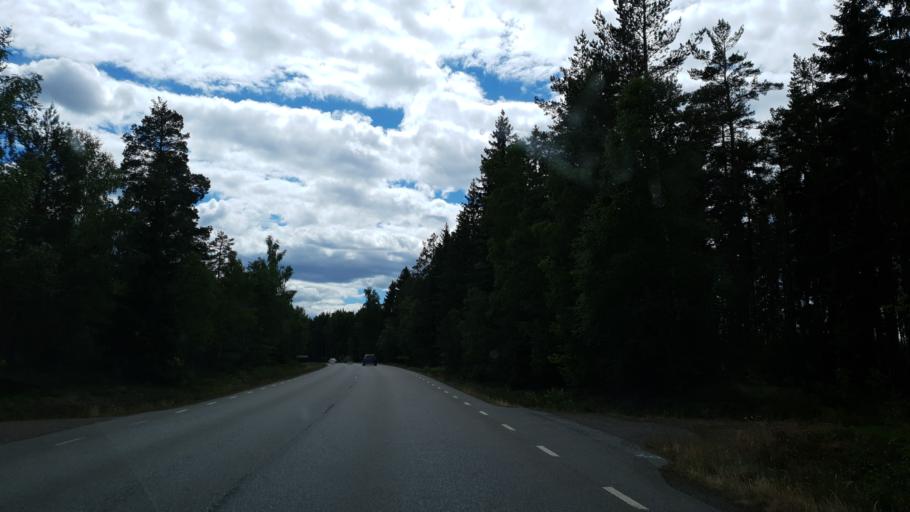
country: SE
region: Kalmar
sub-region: Emmaboda Kommun
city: Emmaboda
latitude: 56.9265
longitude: 15.5732
